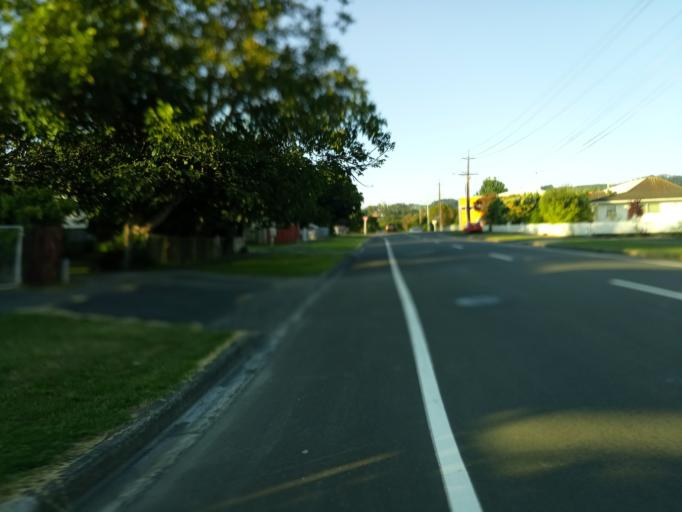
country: NZ
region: Gisborne
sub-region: Gisborne District
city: Gisborne
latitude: -38.6533
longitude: 178.0111
